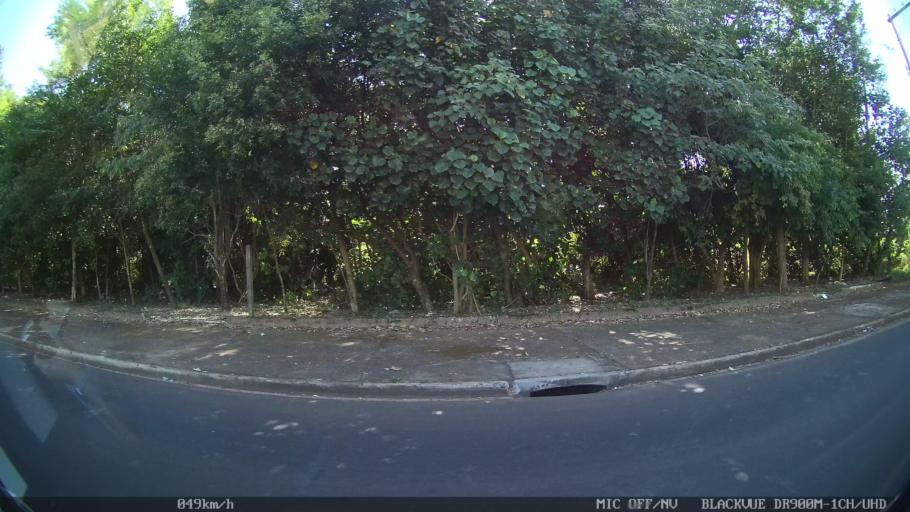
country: BR
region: Sao Paulo
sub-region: Batatais
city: Batatais
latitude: -20.8818
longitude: -47.5903
